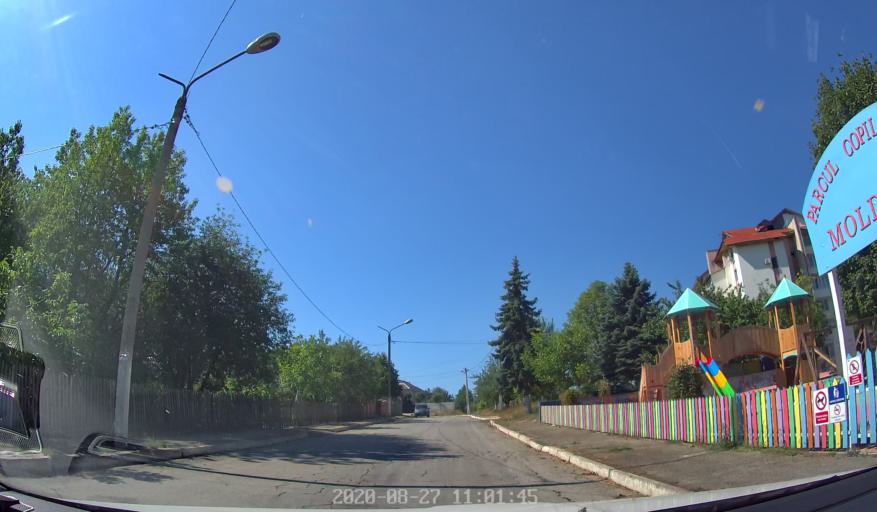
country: MD
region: Laloveni
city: Ialoveni
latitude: 46.9602
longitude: 28.7547
